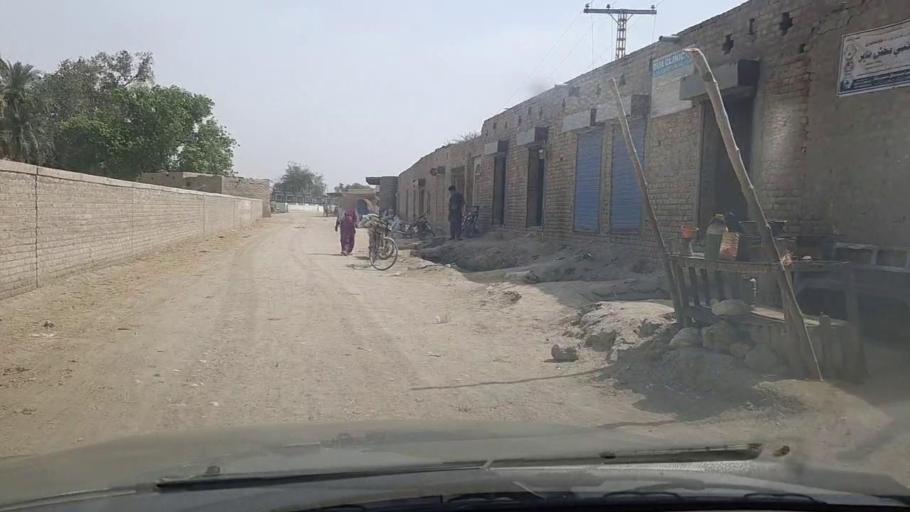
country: PK
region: Sindh
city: Lakhi
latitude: 27.9112
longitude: 68.6880
